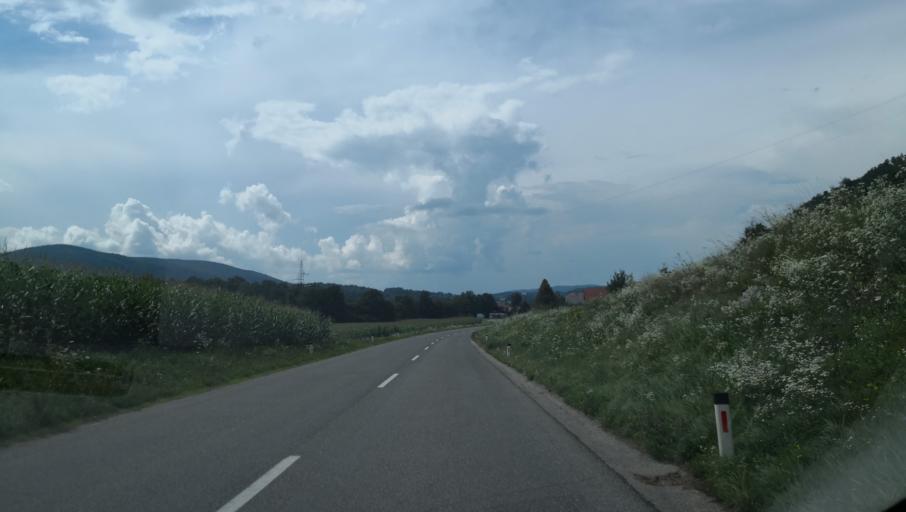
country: SI
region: Zuzemberk
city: Zuzemberk
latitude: 45.8039
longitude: 14.9732
